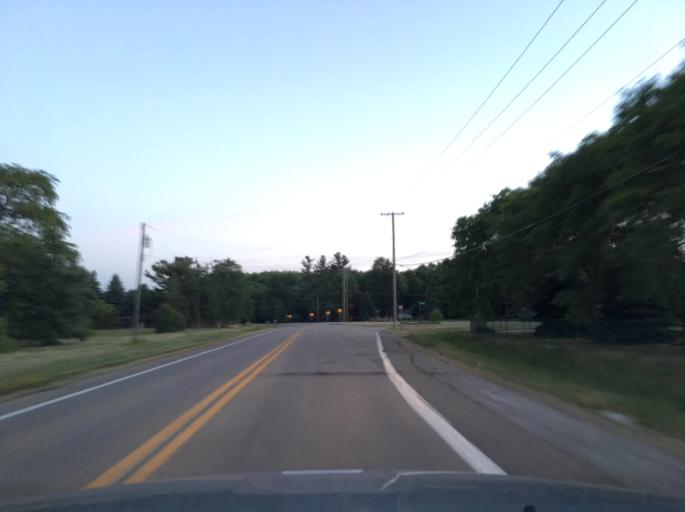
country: US
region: Michigan
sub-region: Macomb County
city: Mount Clemens
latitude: 42.6266
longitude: -82.8876
